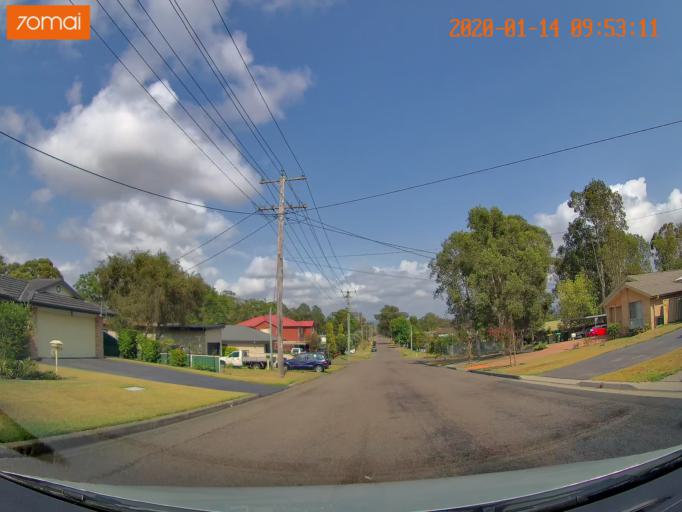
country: AU
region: New South Wales
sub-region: Lake Macquarie Shire
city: Dora Creek
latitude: -33.1090
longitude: 151.5292
